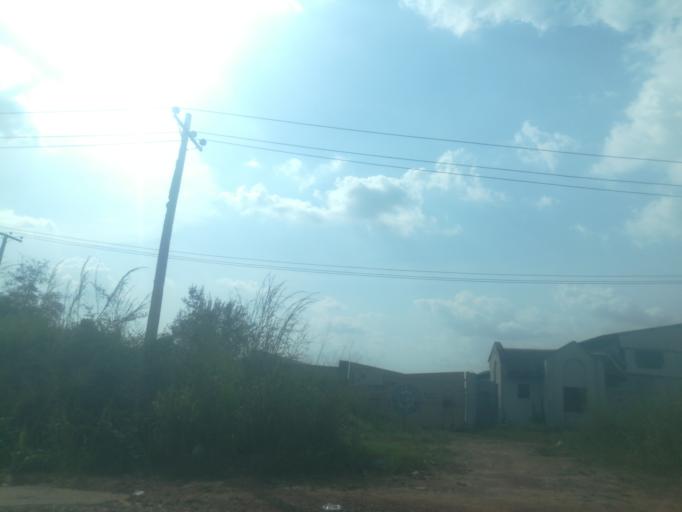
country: NG
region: Ogun
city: Abeokuta
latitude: 7.1132
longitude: 3.2974
